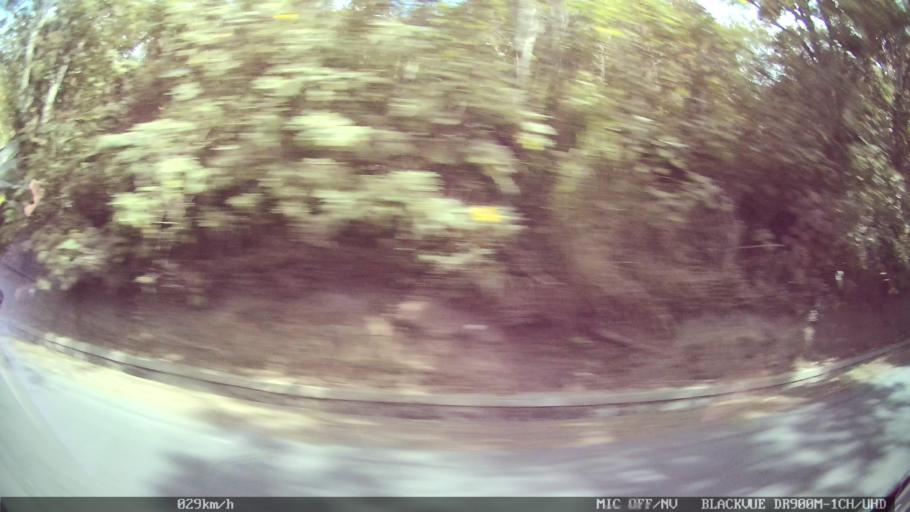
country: ID
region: Bali
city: Banjar Kedisan
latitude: -8.2828
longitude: 115.3653
